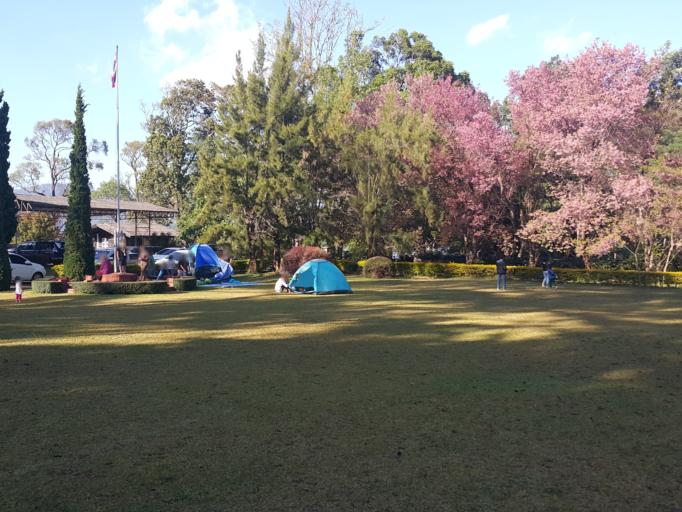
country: TH
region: Chiang Mai
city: Mae Chaem
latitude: 18.6277
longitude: 98.5074
